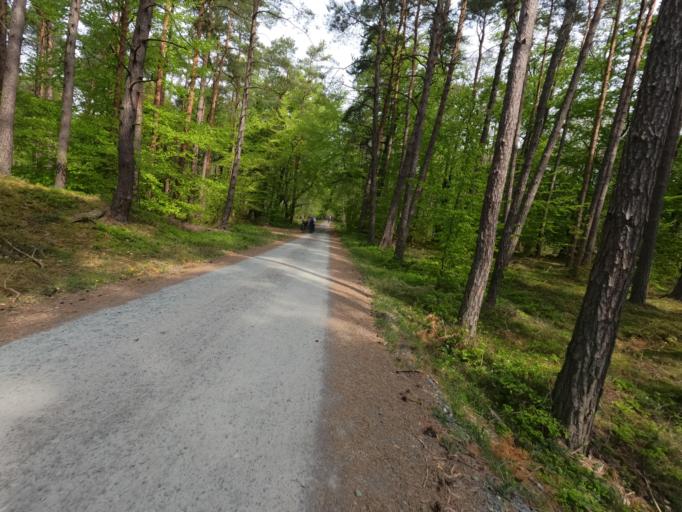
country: DE
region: Mecklenburg-Vorpommern
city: Ostseebad Prerow
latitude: 54.4609
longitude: 12.5146
